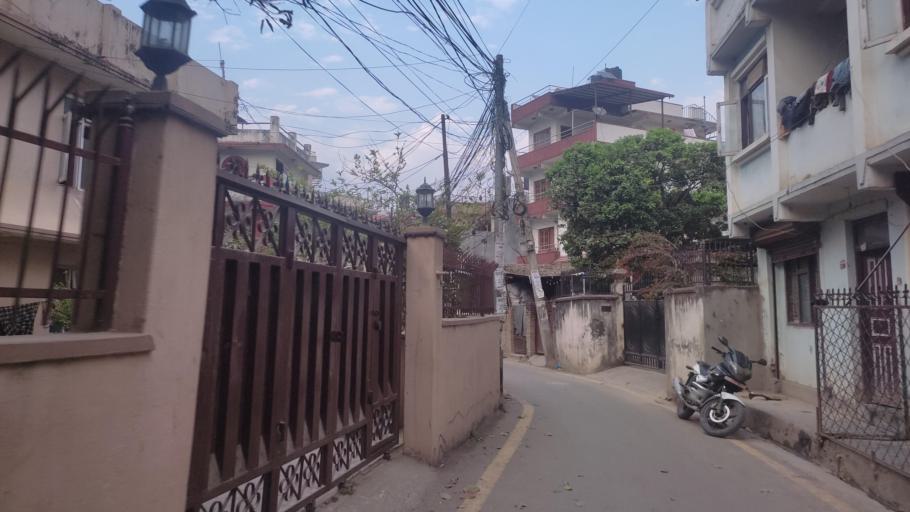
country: NP
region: Central Region
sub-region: Bagmati Zone
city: Patan
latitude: 27.6811
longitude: 85.2965
